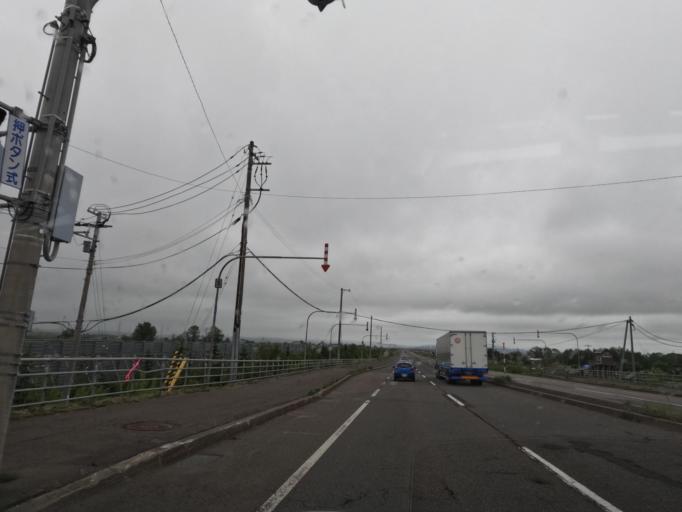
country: JP
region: Hokkaido
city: Tobetsu
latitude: 43.1640
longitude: 141.5200
